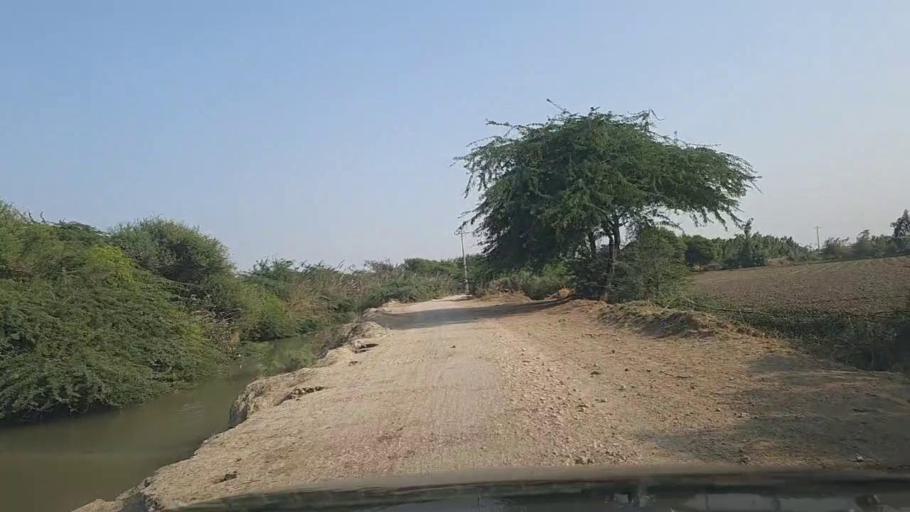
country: PK
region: Sindh
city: Mirpur Sakro
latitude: 24.6338
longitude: 67.7550
